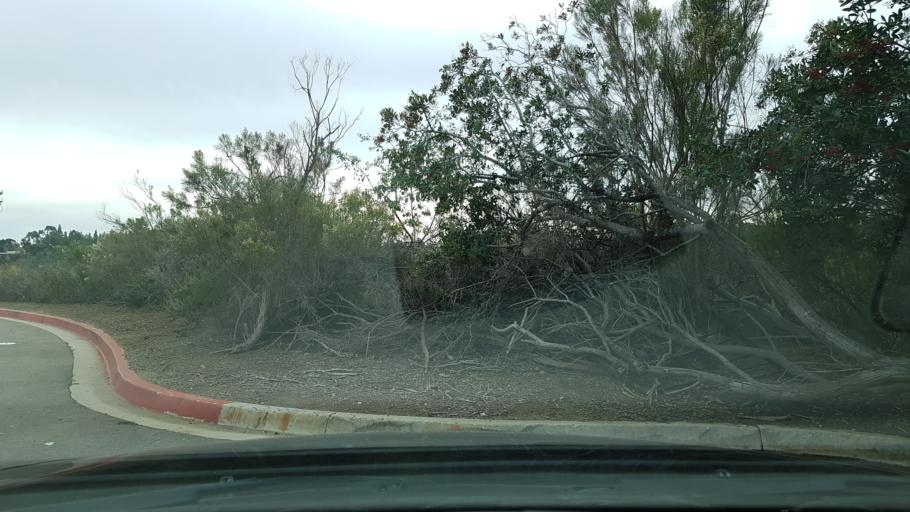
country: US
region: California
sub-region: San Diego County
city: Escondido
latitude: 33.0469
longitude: -117.0776
